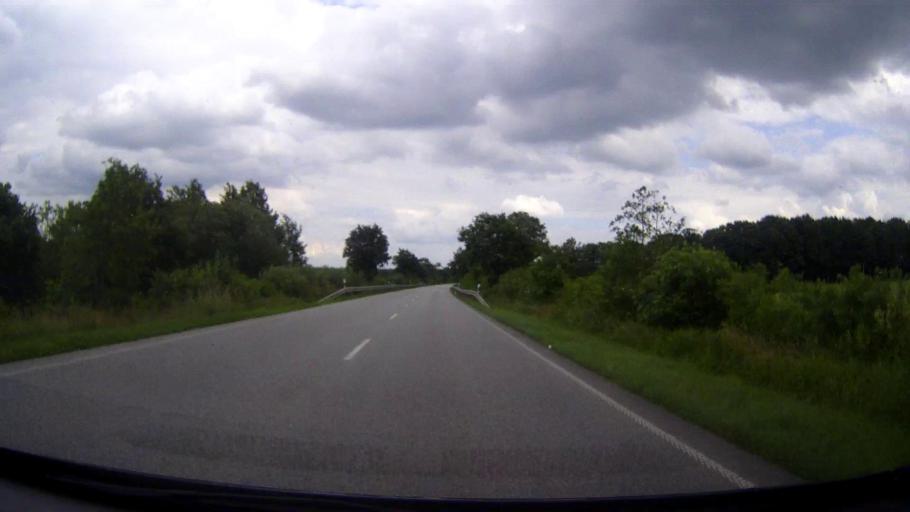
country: DE
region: Schleswig-Holstein
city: Wapelfeld
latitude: 54.0785
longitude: 9.6053
